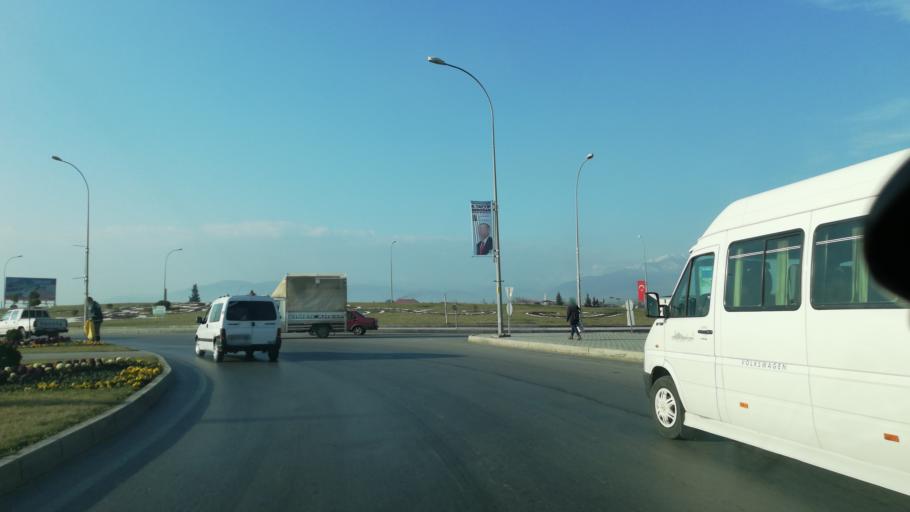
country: TR
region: Kahramanmaras
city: Kahramanmaras
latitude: 37.5685
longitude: 36.9245
